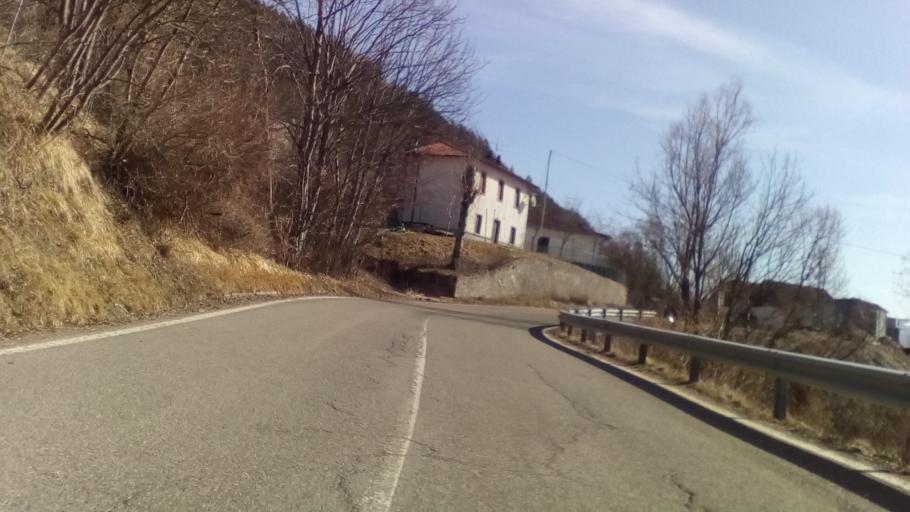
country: IT
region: Emilia-Romagna
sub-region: Provincia di Modena
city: Riolunato
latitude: 44.2579
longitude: 10.6438
